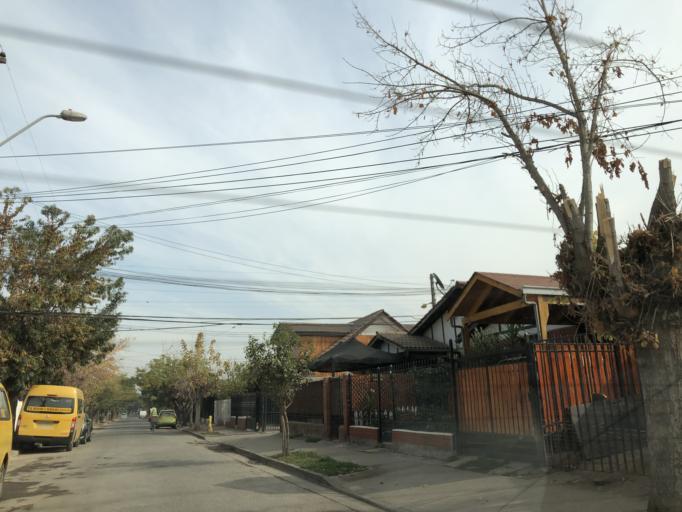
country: CL
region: Santiago Metropolitan
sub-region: Provincia de Cordillera
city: Puente Alto
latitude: -33.5745
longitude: -70.5685
